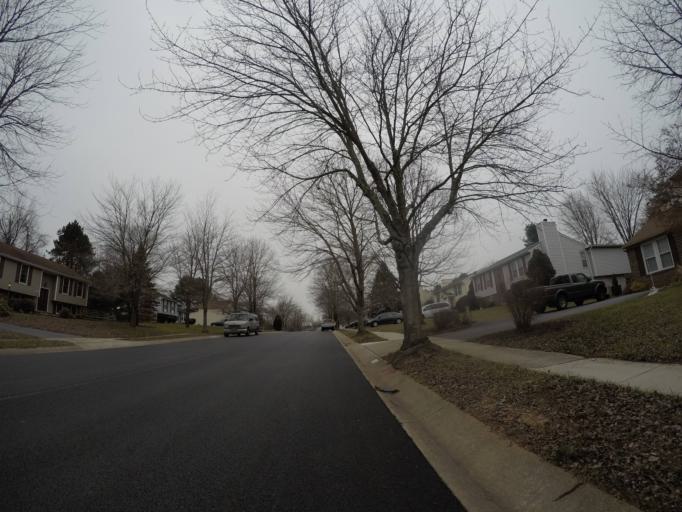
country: US
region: Maryland
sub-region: Howard County
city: Ilchester
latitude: 39.2179
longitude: -76.7892
